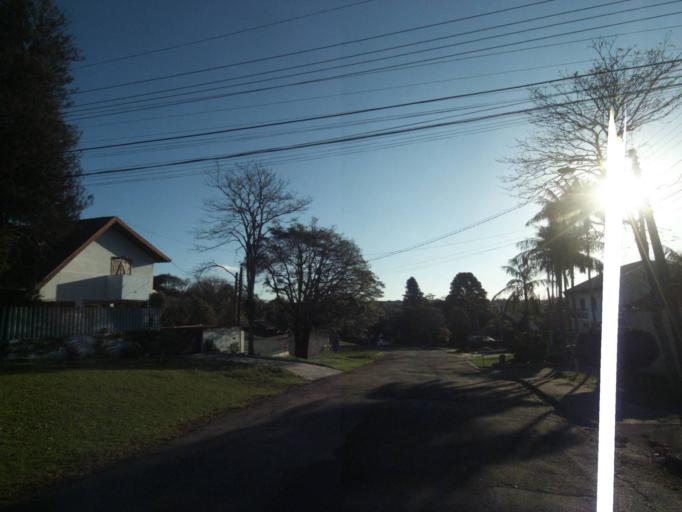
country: BR
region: Parana
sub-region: Curitiba
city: Curitiba
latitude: -25.3773
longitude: -49.2514
